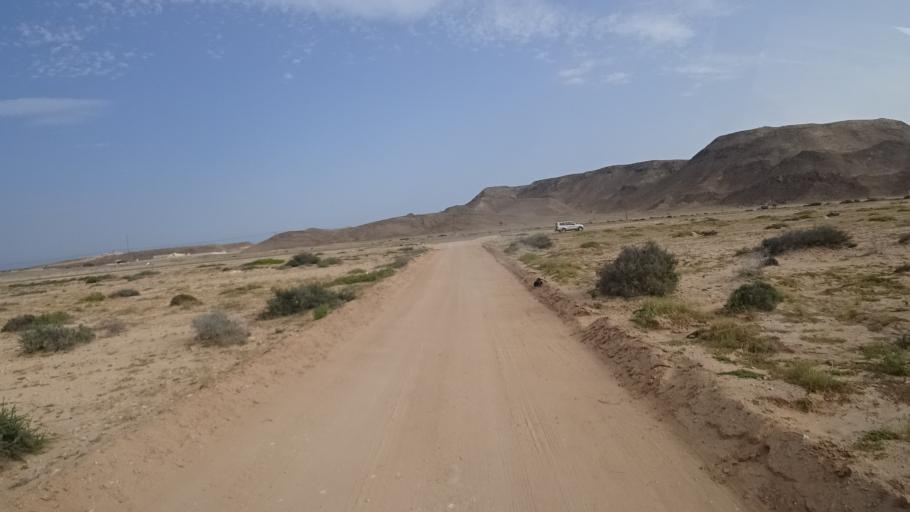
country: OM
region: Ash Sharqiyah
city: Sur
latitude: 22.4361
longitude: 59.8177
